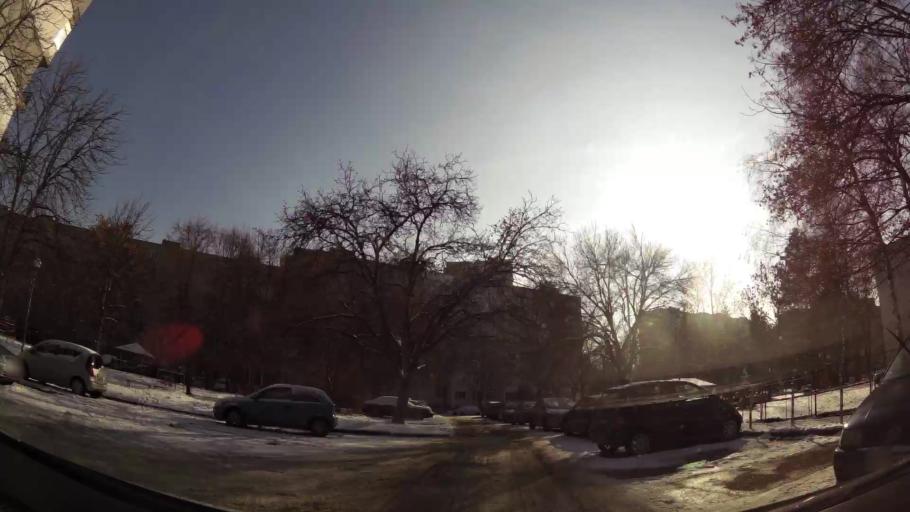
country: BG
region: Sofia-Capital
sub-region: Stolichna Obshtina
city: Sofia
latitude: 42.6634
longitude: 23.3514
